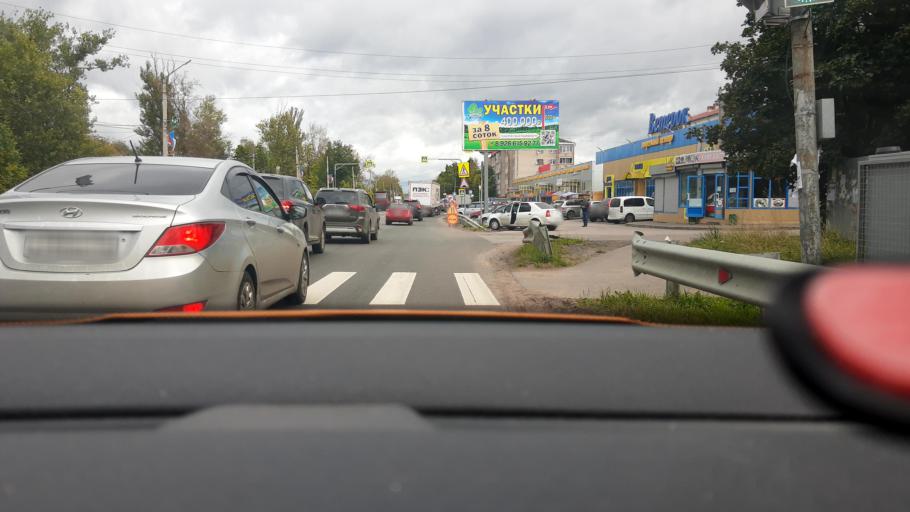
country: RU
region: Moskovskaya
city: Kostino
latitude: 56.0444
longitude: 37.9790
